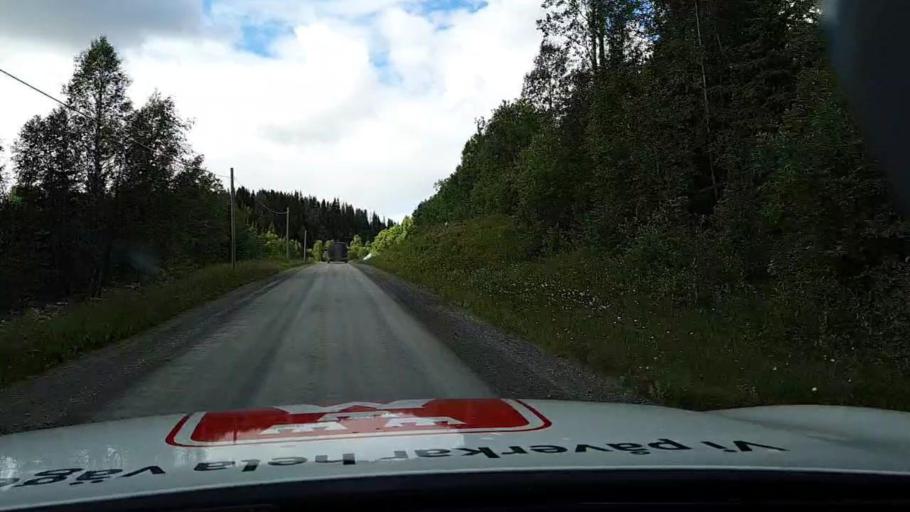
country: SE
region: Jaemtland
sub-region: Krokoms Kommun
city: Valla
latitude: 63.7143
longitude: 13.5295
